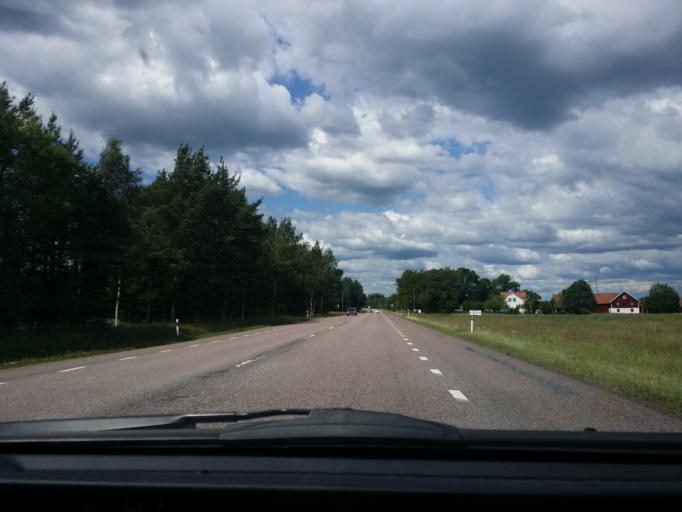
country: SE
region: OErebro
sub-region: Orebro Kommun
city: Hovsta
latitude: 59.4278
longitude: 15.1721
